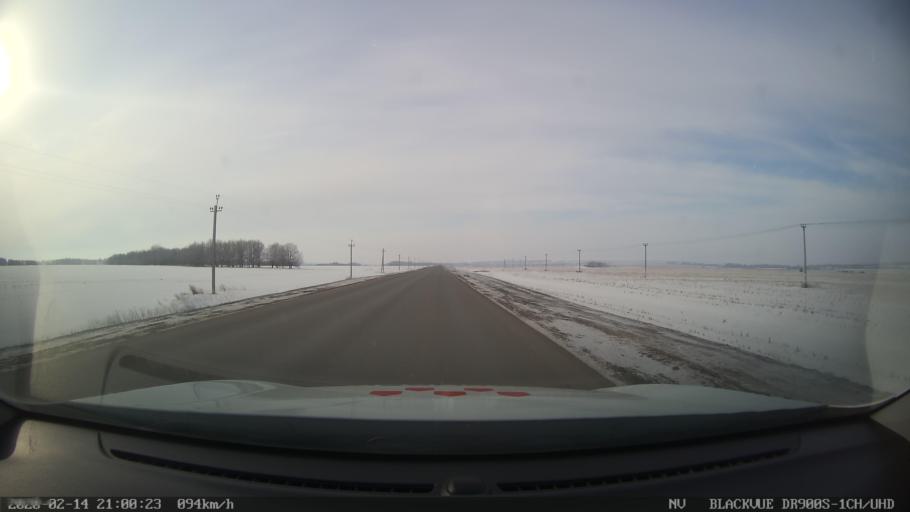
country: RU
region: Tatarstan
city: Kuybyshevskiy Zaton
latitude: 55.1715
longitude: 49.2209
